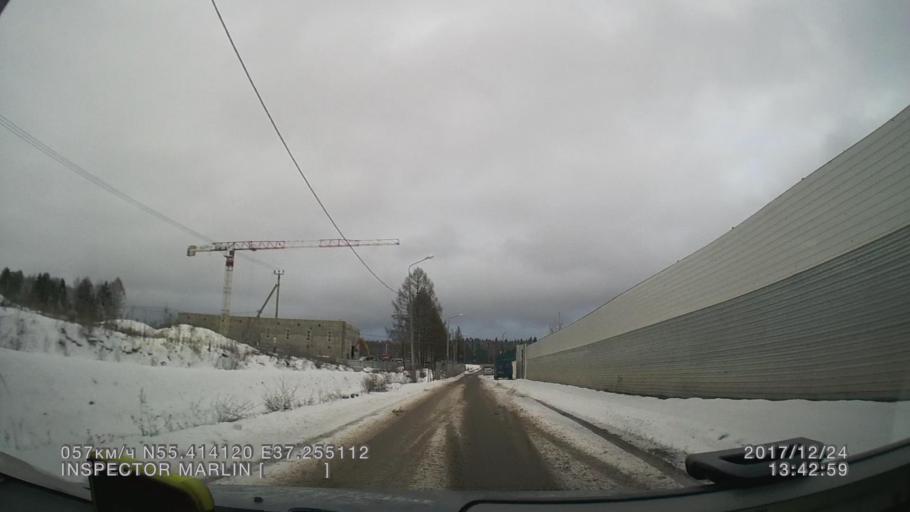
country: RU
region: Moskovskaya
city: Troitsk
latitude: 55.4141
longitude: 37.2551
